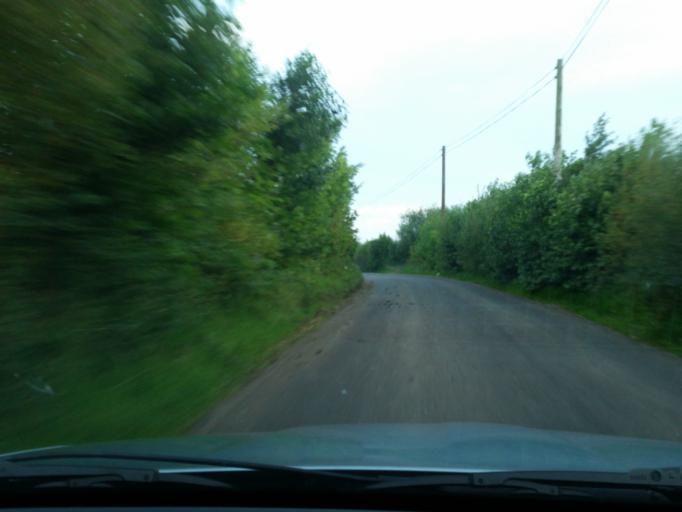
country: GB
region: Northern Ireland
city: Fivemiletown
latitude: 54.3114
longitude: -7.2964
